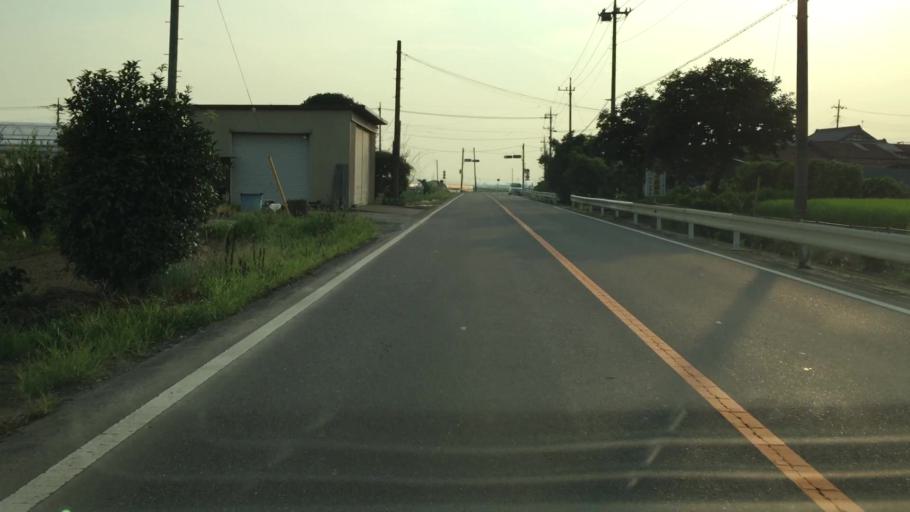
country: JP
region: Tochigi
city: Fujioka
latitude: 36.2486
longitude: 139.6061
